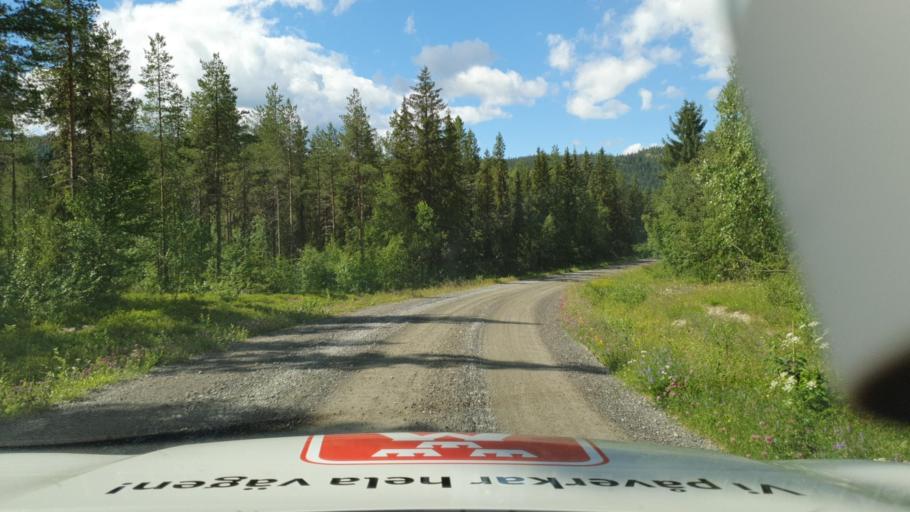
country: SE
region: Vaesterbotten
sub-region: Sorsele Kommun
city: Sorsele
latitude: 65.6418
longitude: 17.4134
